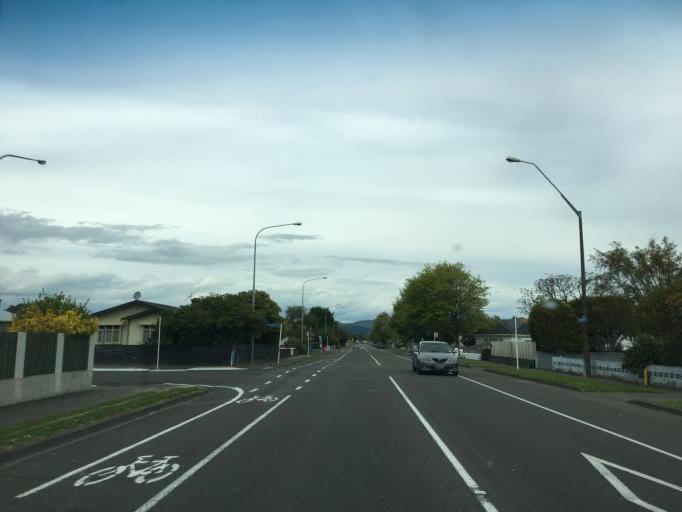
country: NZ
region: Manawatu-Wanganui
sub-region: Palmerston North City
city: Palmerston North
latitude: -40.3597
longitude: 175.5915
